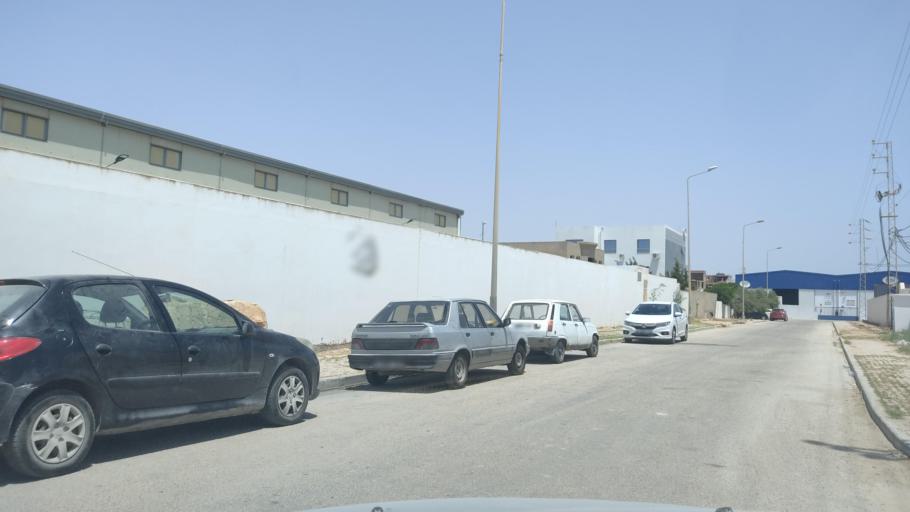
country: TN
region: Safaqis
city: Sfax
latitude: 34.6649
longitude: 10.6966
